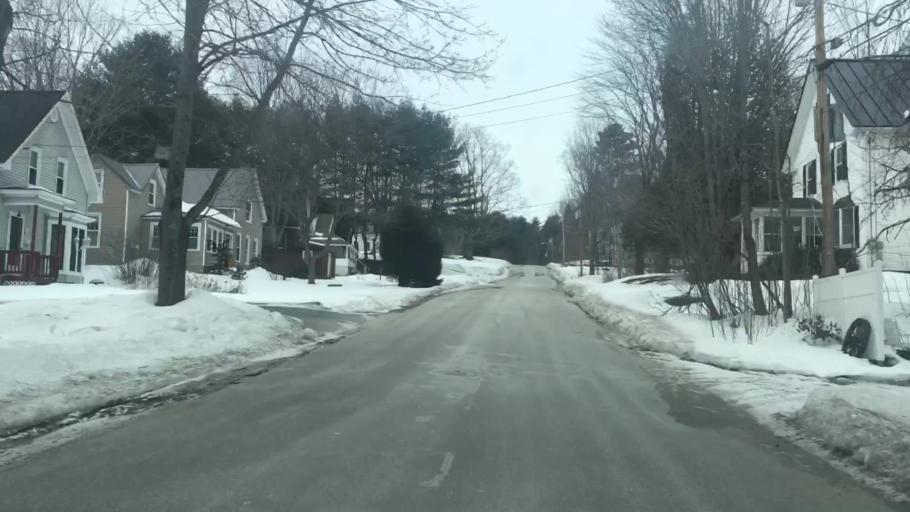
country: US
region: Maine
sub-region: Kennebec County
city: Winthrop
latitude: 44.3063
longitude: -69.9801
